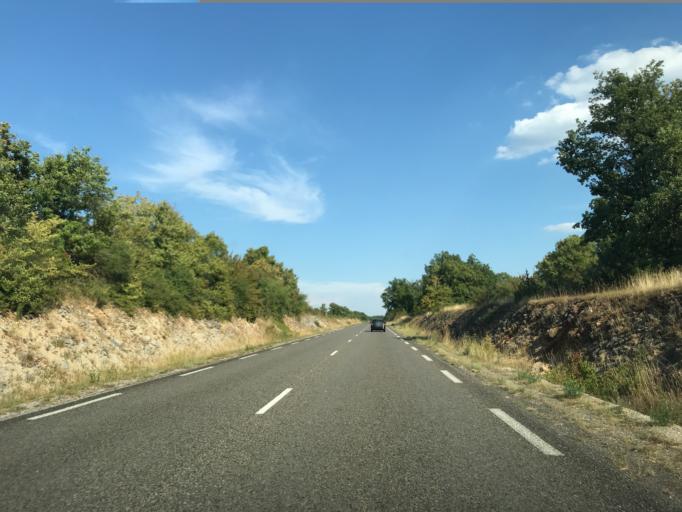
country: FR
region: Midi-Pyrenees
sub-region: Departement du Lot
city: Gramat
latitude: 44.6826
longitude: 1.6201
